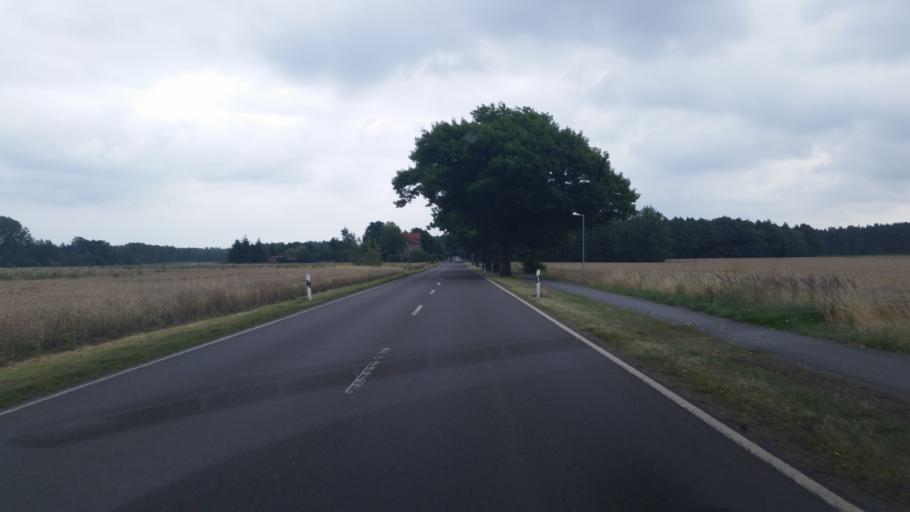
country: DE
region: Brandenburg
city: Hohenbocka
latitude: 51.4632
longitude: 14.0764
